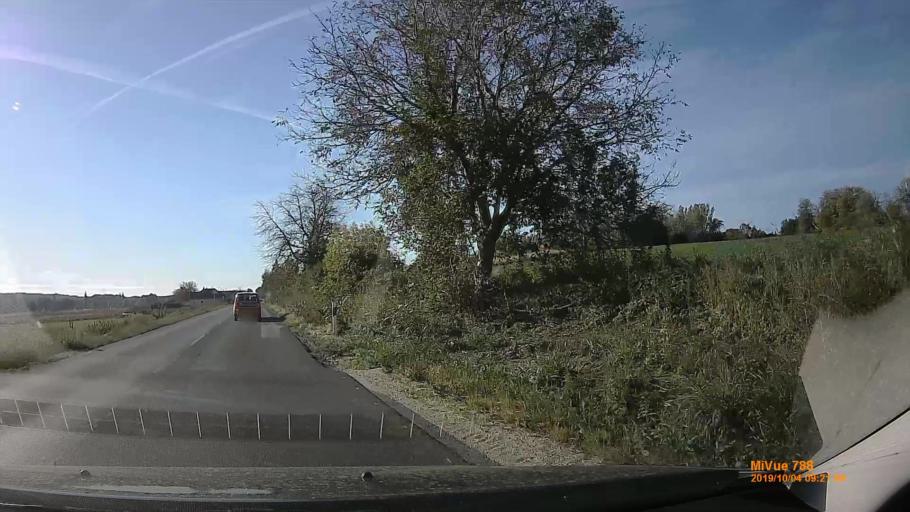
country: HU
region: Somogy
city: Karad
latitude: 46.5578
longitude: 17.8104
